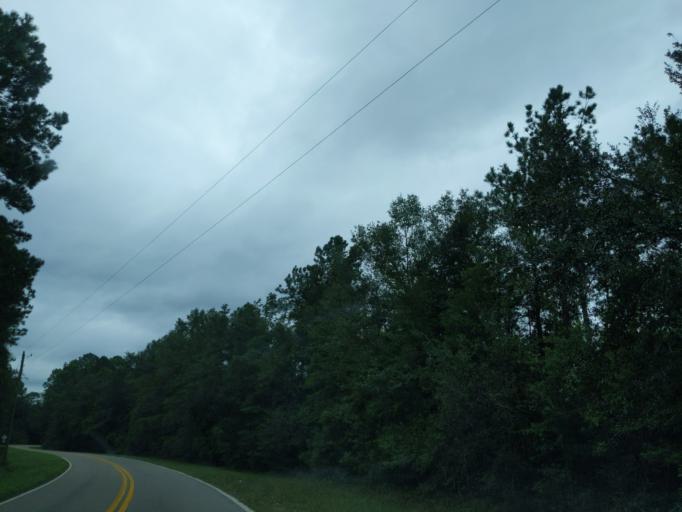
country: US
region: Florida
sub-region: Gadsden County
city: Midway
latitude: 30.4131
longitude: -84.4181
